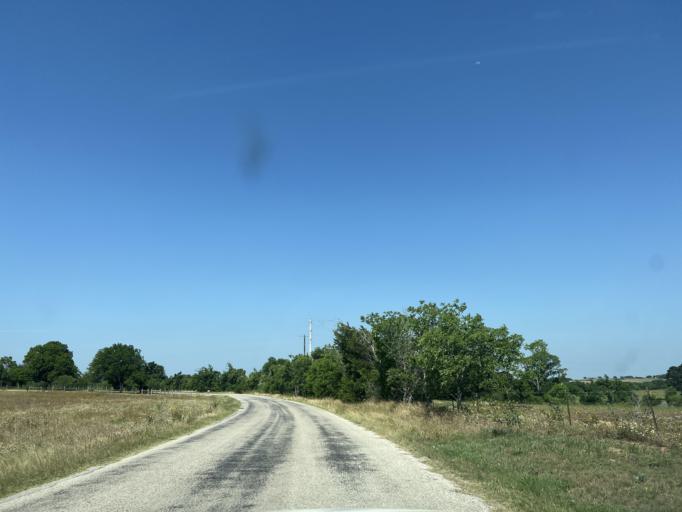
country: US
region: Texas
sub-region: Washington County
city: Brenham
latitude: 30.1732
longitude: -96.3573
